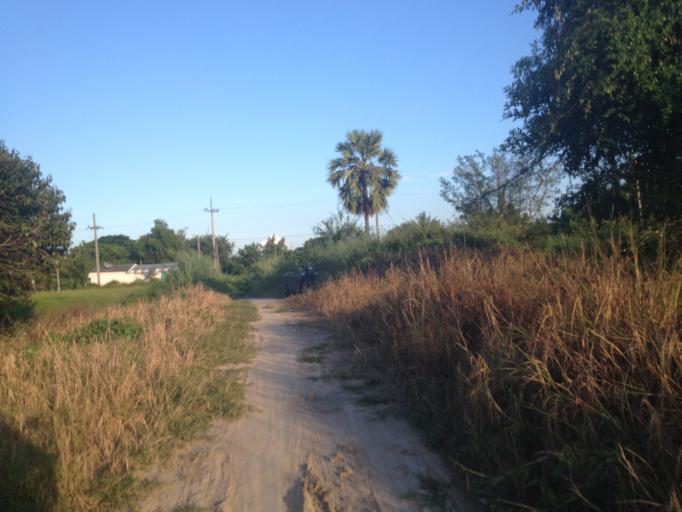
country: TH
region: Chiang Mai
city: Hang Dong
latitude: 18.6795
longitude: 98.9041
